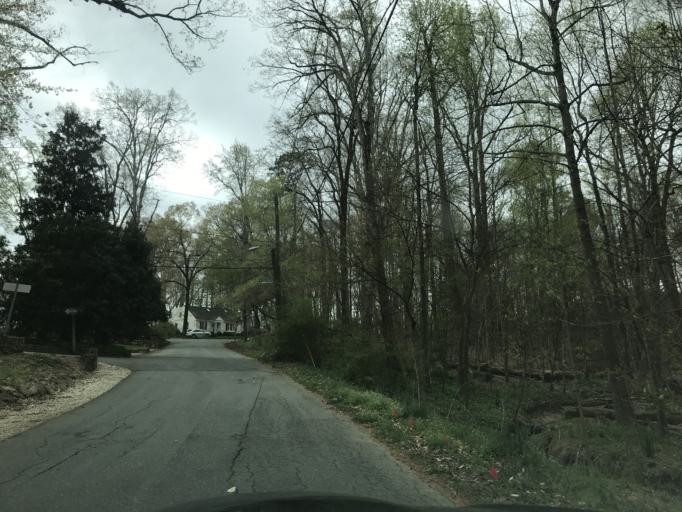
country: US
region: North Carolina
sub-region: Orange County
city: Chapel Hill
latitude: 35.9132
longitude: -79.0415
